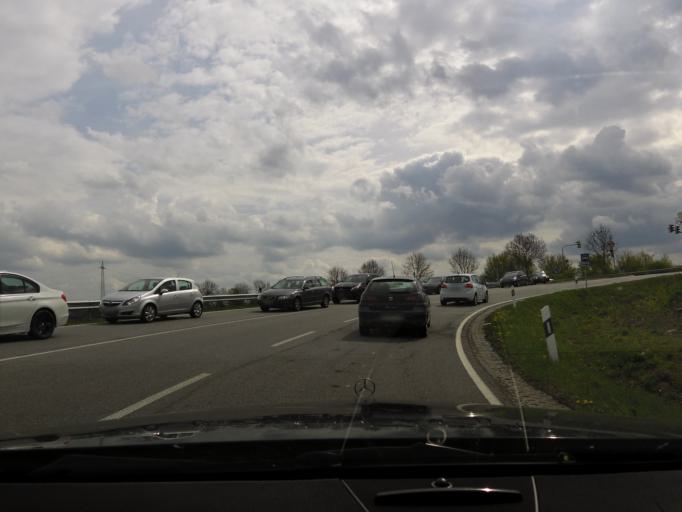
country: DE
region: Bavaria
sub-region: Lower Bavaria
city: Ergolding
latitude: 48.5657
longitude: 12.1436
